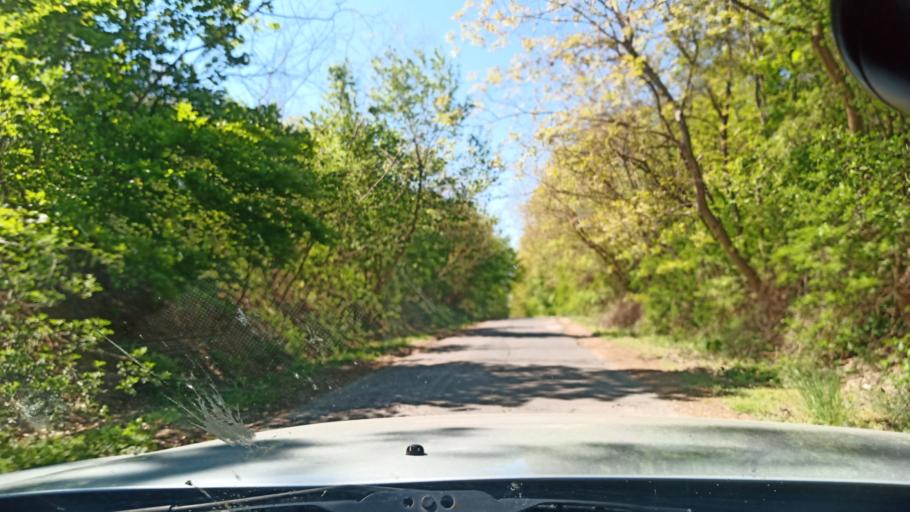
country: HU
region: Zala
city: Heviz
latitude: 46.7644
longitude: 17.1625
